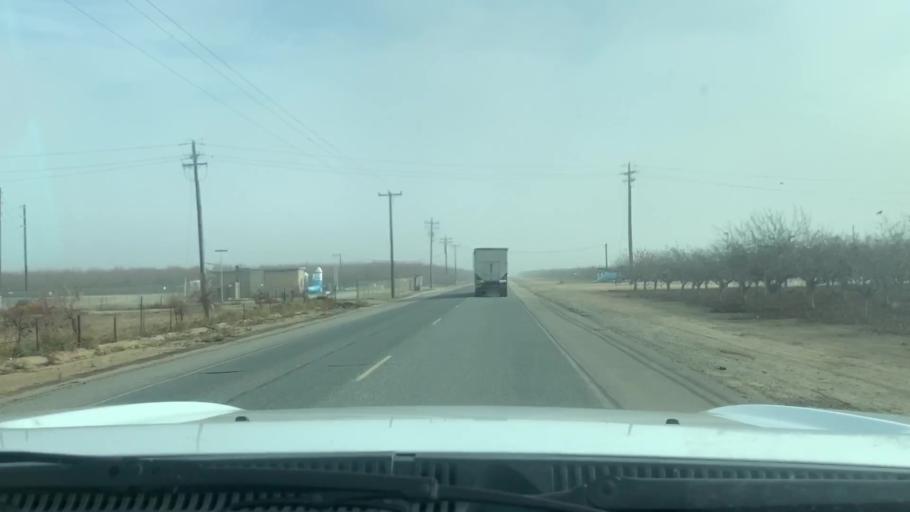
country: US
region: California
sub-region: Kern County
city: Buttonwillow
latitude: 35.5006
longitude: -119.4939
